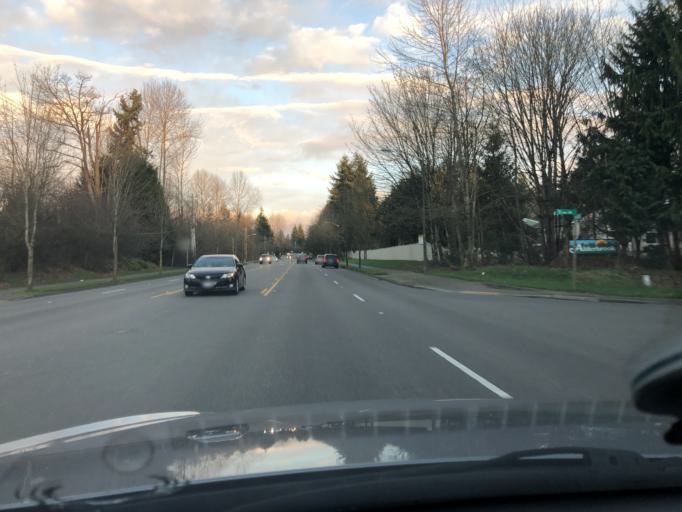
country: US
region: Washington
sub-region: King County
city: Federal Way
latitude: 47.3152
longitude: -122.3521
